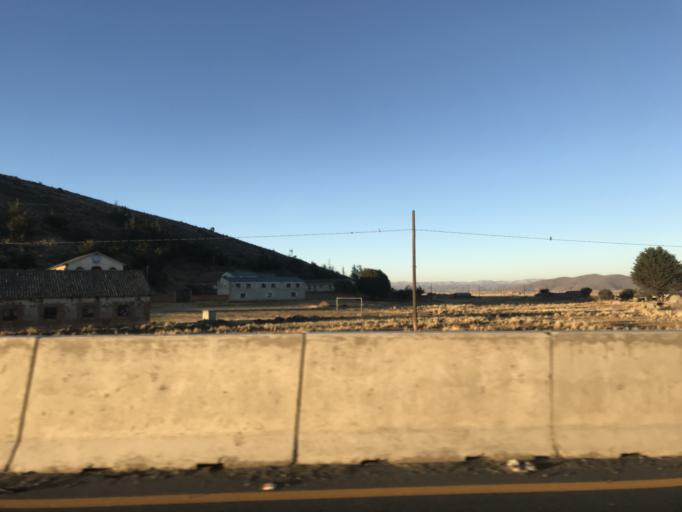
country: BO
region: La Paz
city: Batallas
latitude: -16.3005
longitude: -68.4889
